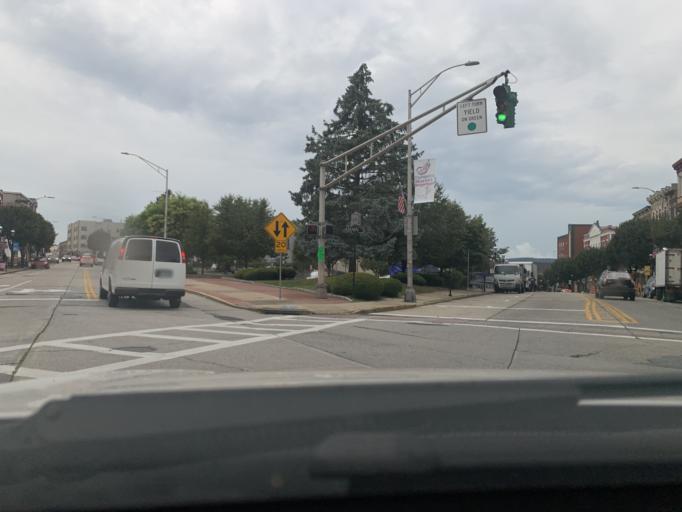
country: US
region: New York
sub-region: Westchester County
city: Ossining
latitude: 41.1611
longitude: -73.8635
